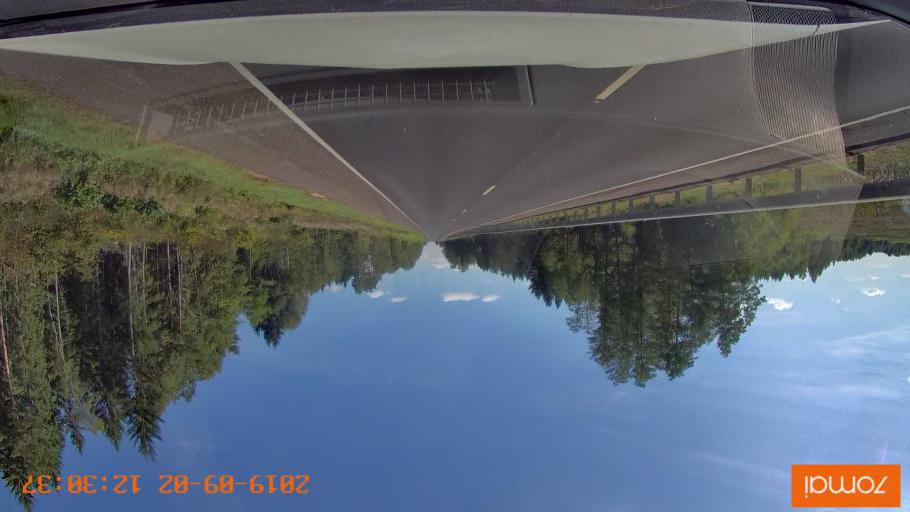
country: RU
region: Smolensk
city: Shumyachi
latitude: 53.8308
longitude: 32.4703
